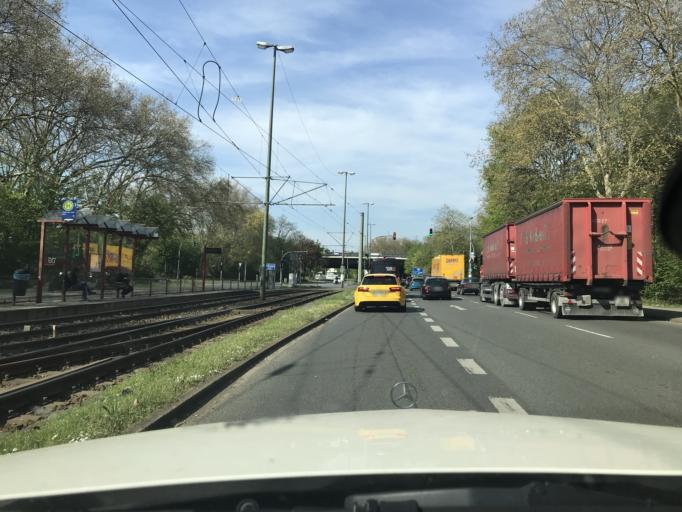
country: DE
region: North Rhine-Westphalia
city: Meiderich
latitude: 51.4826
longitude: 6.7944
